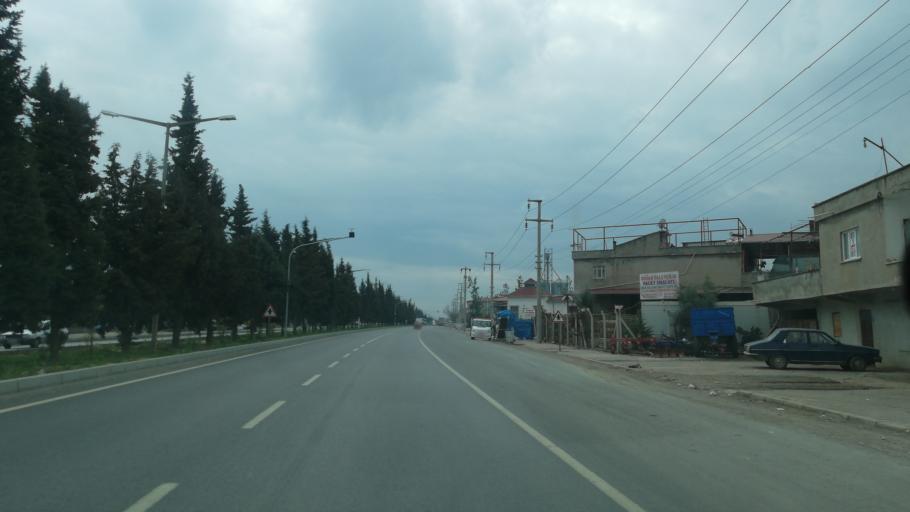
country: TR
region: Kahramanmaras
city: Turkoglu
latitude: 37.4156
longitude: 36.8808
